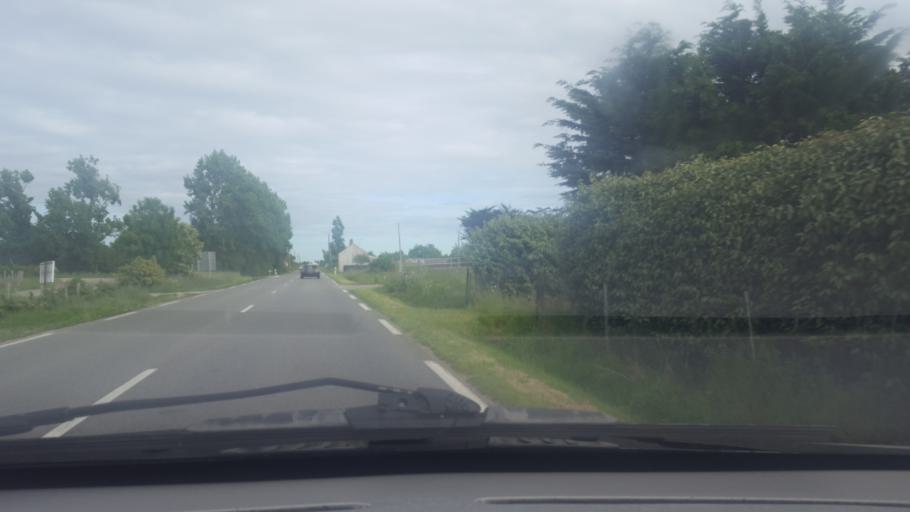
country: FR
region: Pays de la Loire
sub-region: Departement de la Loire-Atlantique
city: Bourgneuf-en-Retz
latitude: 47.0380
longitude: -1.9397
